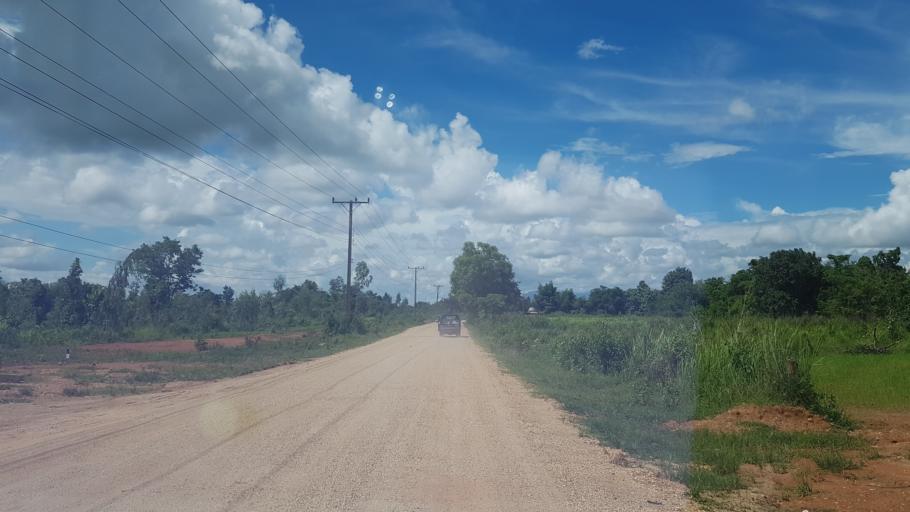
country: LA
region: Vientiane
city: Vientiane
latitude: 18.2296
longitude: 102.5252
